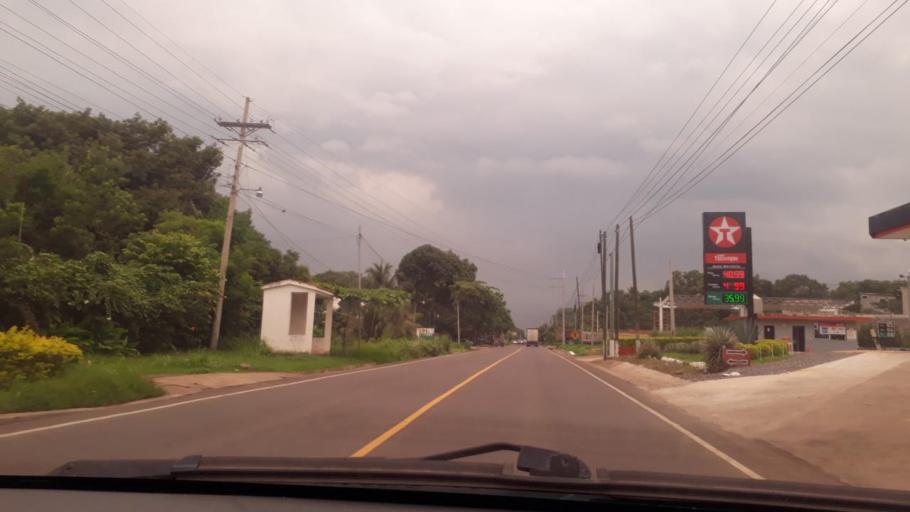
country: GT
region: Santa Rosa
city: Guazacapan
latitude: 14.0669
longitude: -90.4093
